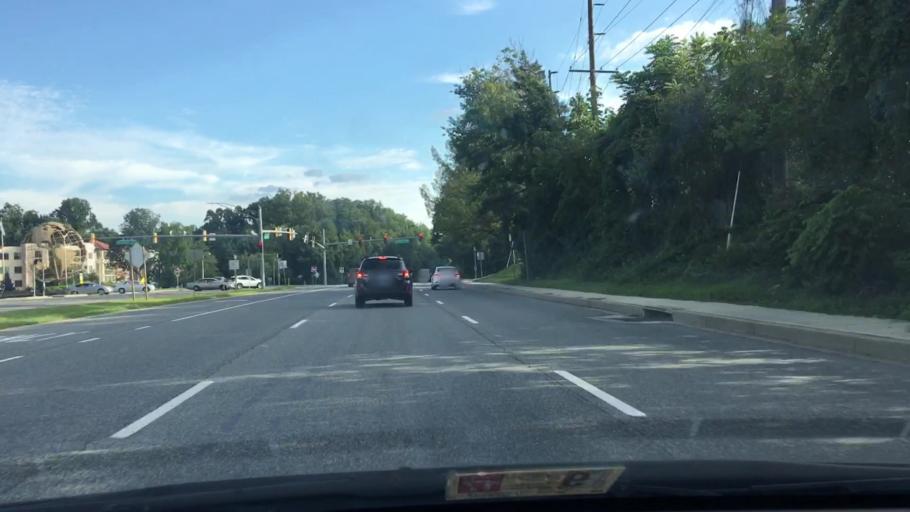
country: US
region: Maryland
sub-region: Montgomery County
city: Rossmoor
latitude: 39.1023
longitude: -77.0771
